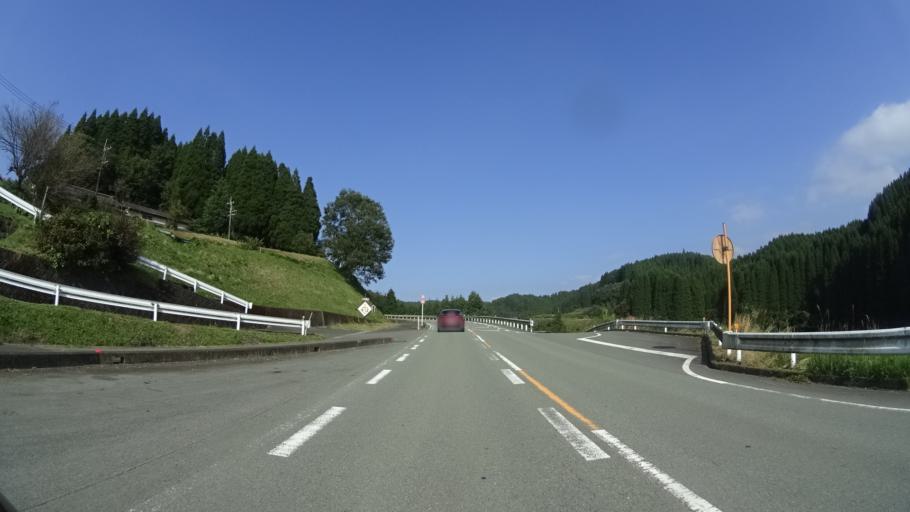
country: JP
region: Oita
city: Tsukawaki
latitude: 33.1422
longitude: 131.1058
